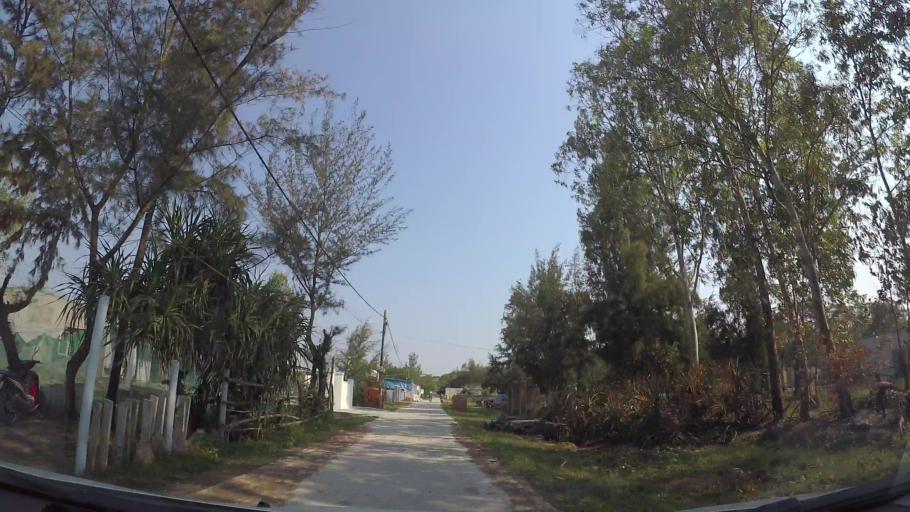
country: VN
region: Quang Nam
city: Quang Nam
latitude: 15.9471
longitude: 108.2707
